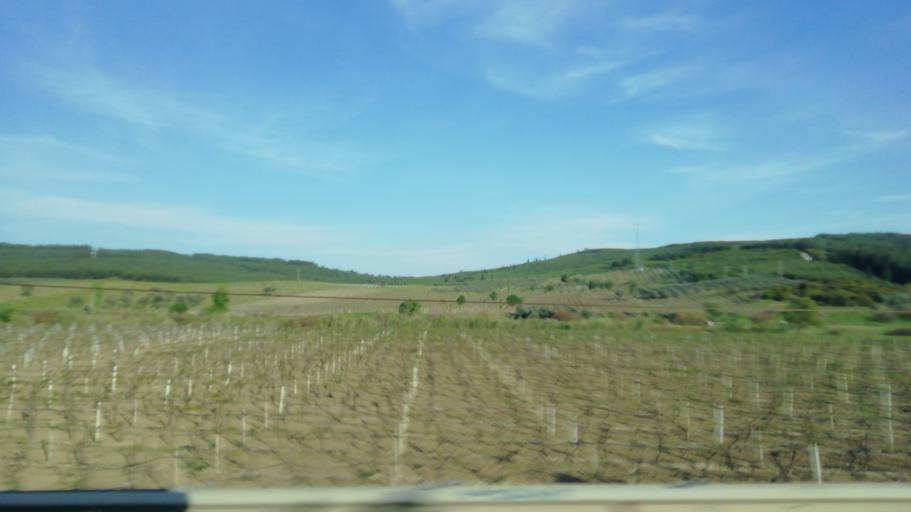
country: TR
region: Manisa
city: Halitpasa
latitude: 38.7955
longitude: 27.6850
